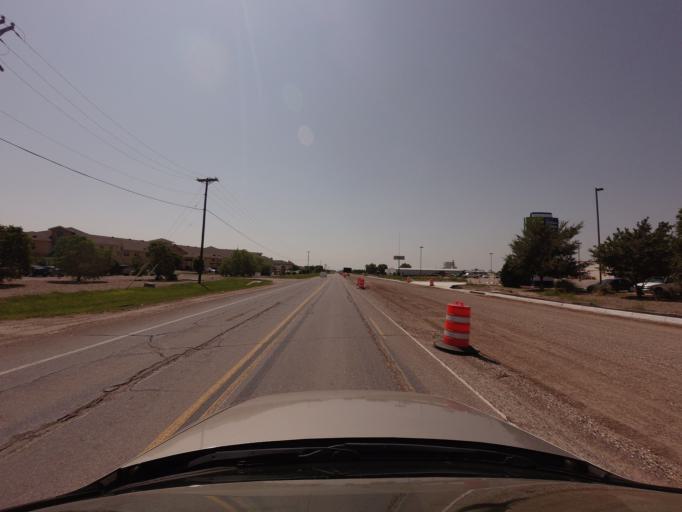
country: US
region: New Mexico
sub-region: Curry County
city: Clovis
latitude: 34.4467
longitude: -103.1964
